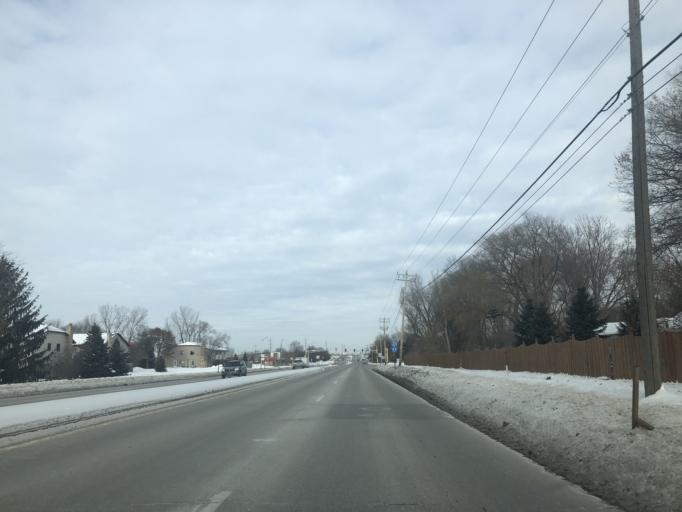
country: US
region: Minnesota
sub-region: Anoka County
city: Lexington
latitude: 45.1510
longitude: -93.1634
